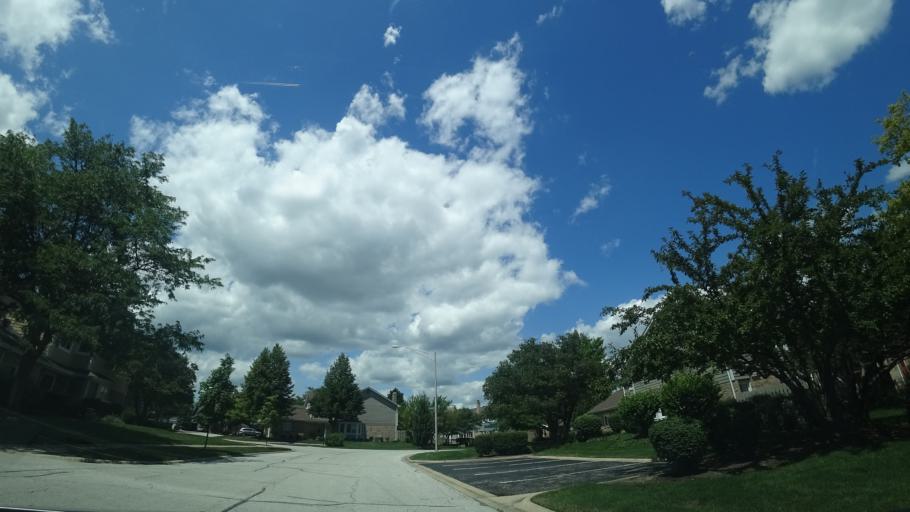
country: US
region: Illinois
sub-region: Will County
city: Mokena
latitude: 41.5750
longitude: -87.8952
